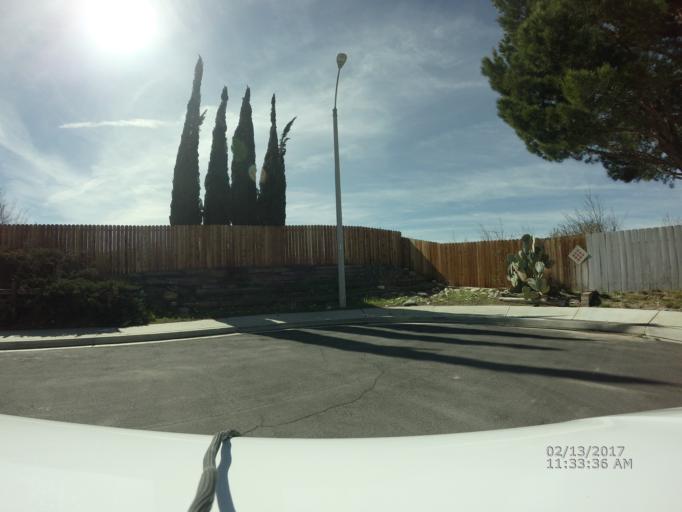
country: US
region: California
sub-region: Los Angeles County
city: Littlerock
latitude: 34.5242
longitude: -118.0011
